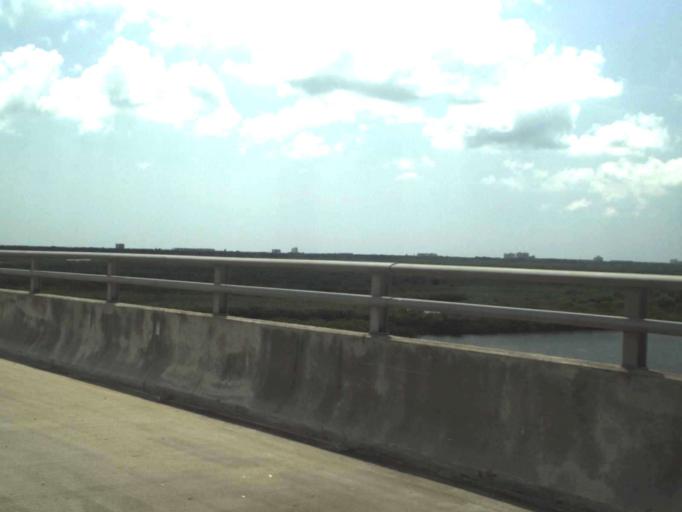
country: US
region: Florida
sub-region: Volusia County
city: New Smyrna Beach
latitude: 29.0236
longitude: -80.9178
